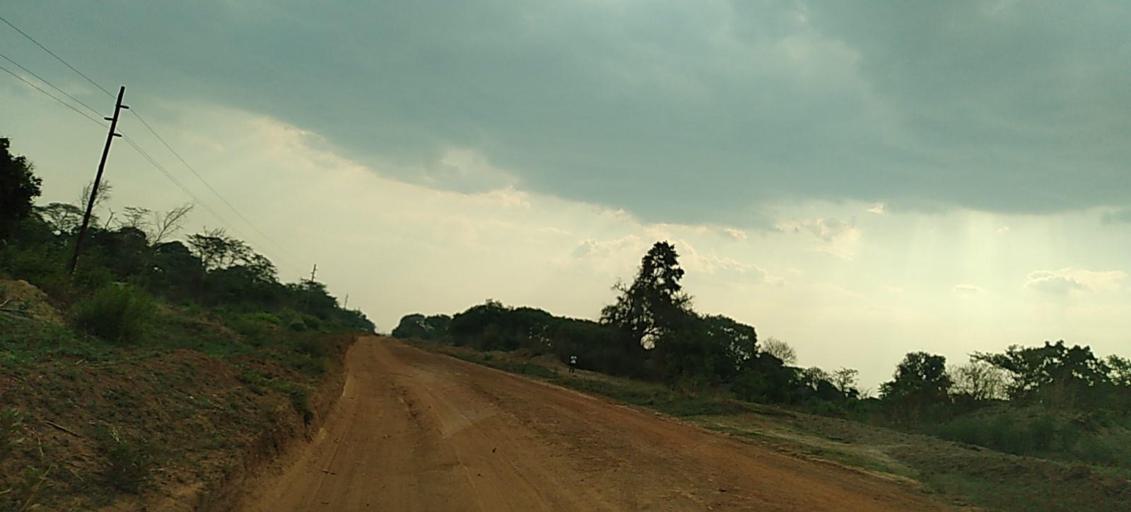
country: ZM
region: Copperbelt
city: Kalulushi
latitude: -12.9387
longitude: 27.9255
